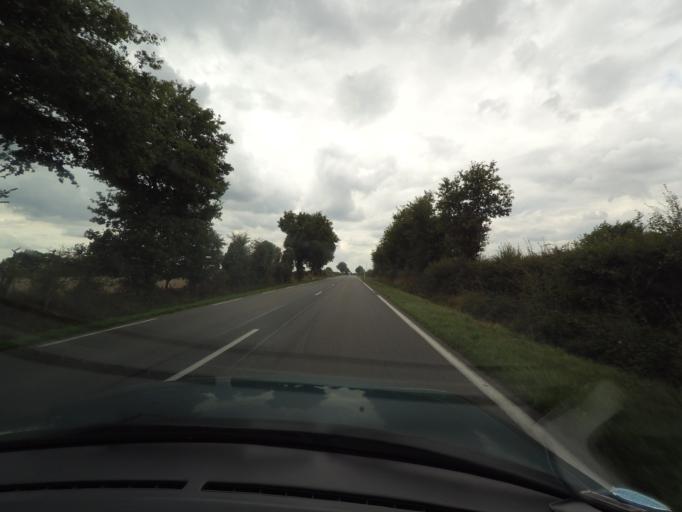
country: FR
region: Poitou-Charentes
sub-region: Departement des Deux-Sevres
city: Thenezay
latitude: 46.6581
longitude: -0.0437
